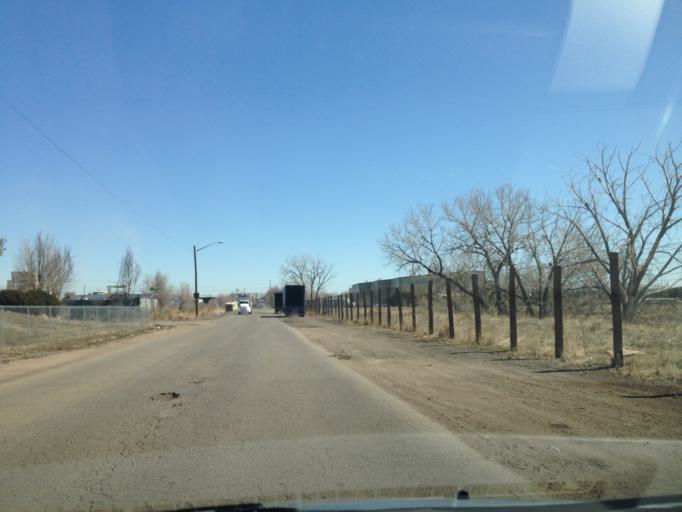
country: US
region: Colorado
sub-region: Adams County
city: Commerce City
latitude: 39.7955
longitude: -104.9733
